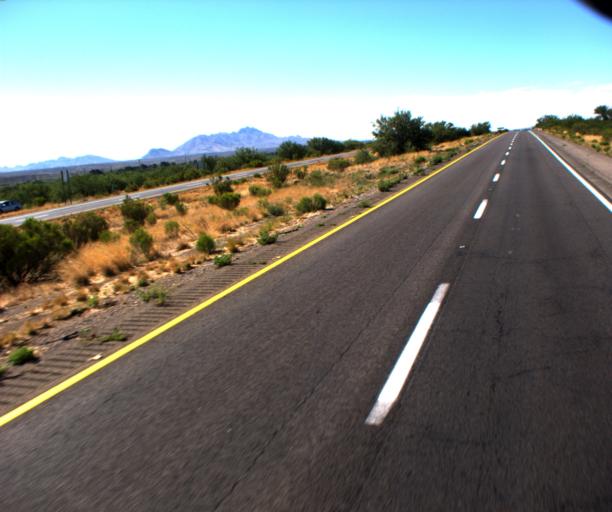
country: US
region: Arizona
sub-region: Santa Cruz County
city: Tubac
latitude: 31.6556
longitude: -111.0603
